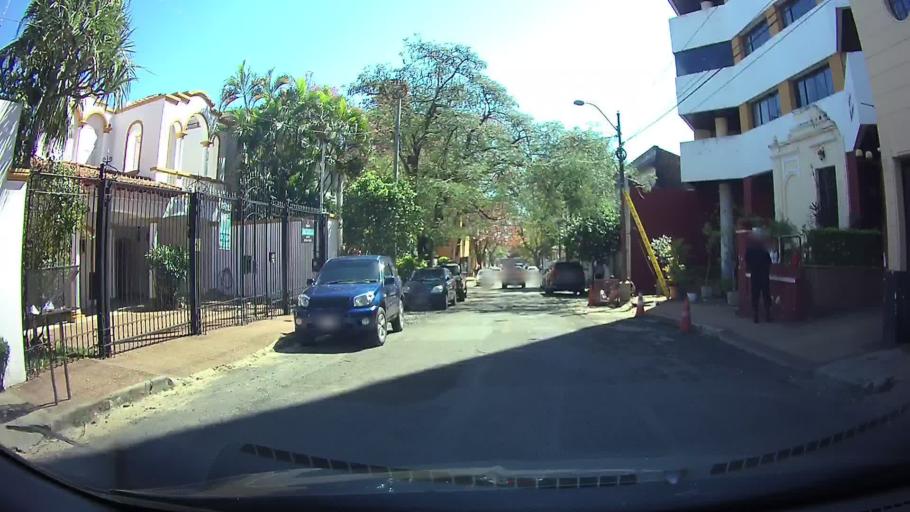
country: PY
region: Asuncion
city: Asuncion
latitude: -25.2836
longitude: -57.6180
